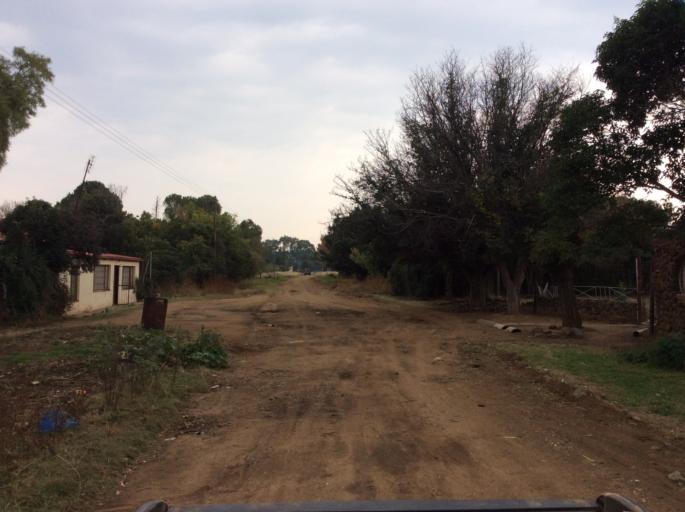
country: LS
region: Mafeteng
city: Mafeteng
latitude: -29.9893
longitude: 27.0182
